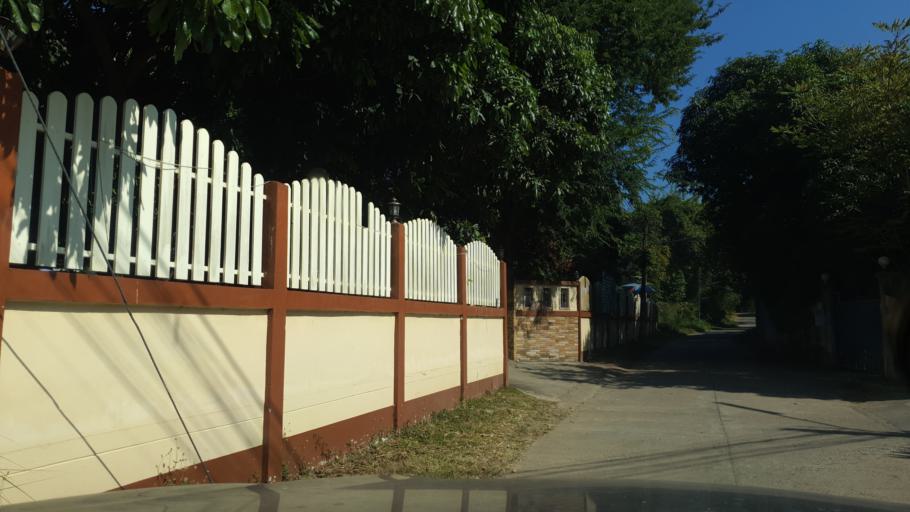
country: TH
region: Chiang Mai
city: San Sai
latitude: 18.8885
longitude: 99.1668
